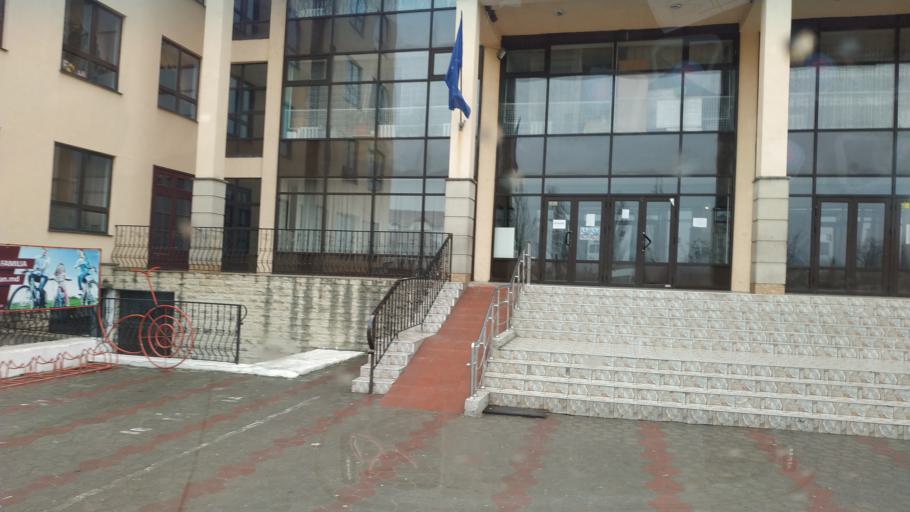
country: MD
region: Chisinau
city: Singera
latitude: 46.9144
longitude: 28.9742
